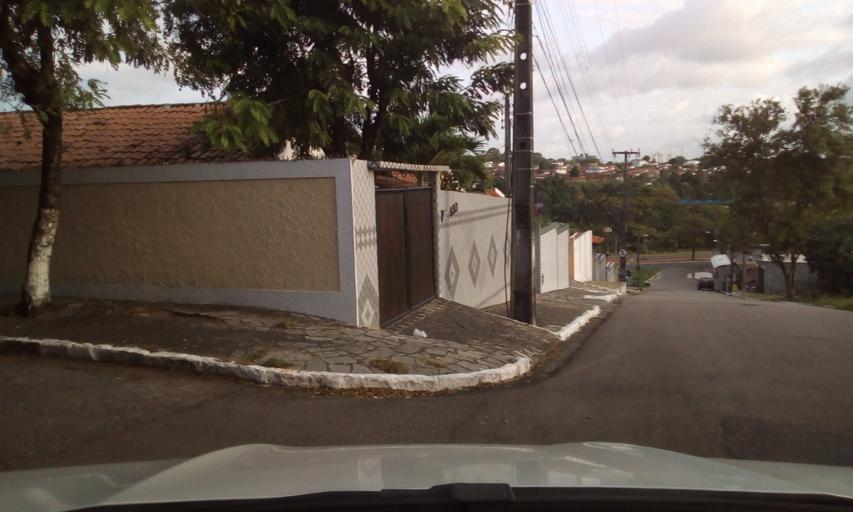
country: BR
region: Paraiba
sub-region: Joao Pessoa
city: Joao Pessoa
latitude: -7.1260
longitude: -34.8514
